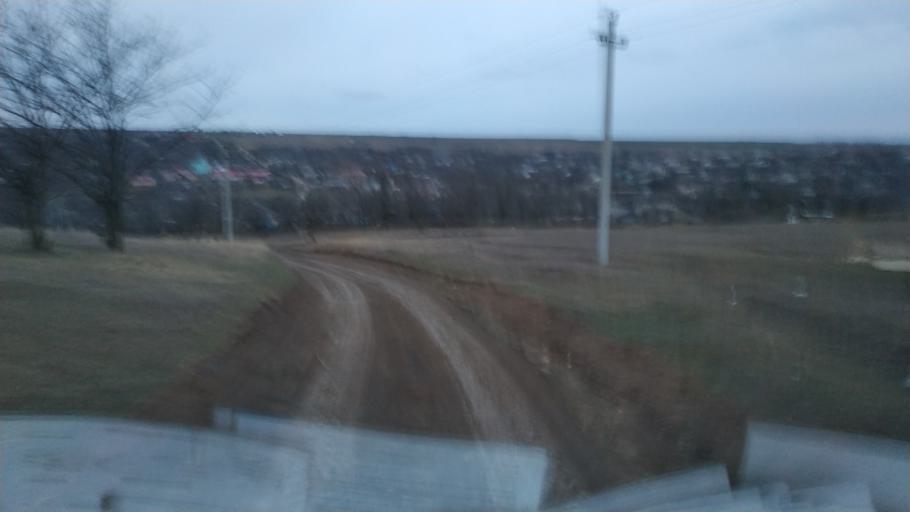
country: MD
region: Causeni
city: Causeni
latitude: 46.5018
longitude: 29.4103
